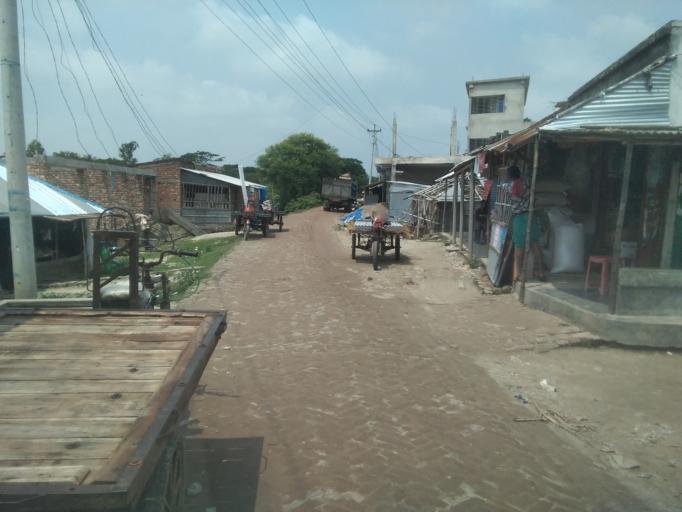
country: BD
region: Khulna
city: Phultala
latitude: 22.6435
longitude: 89.4311
